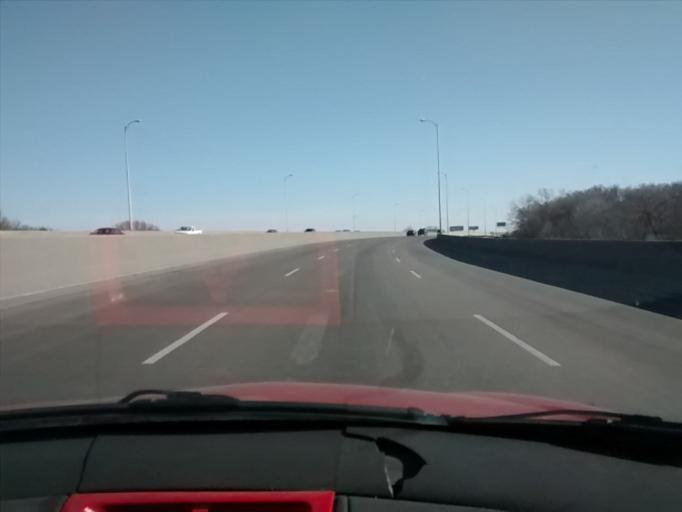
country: US
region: Nebraska
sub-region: Douglas County
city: Omaha
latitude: 41.1966
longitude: -95.9427
